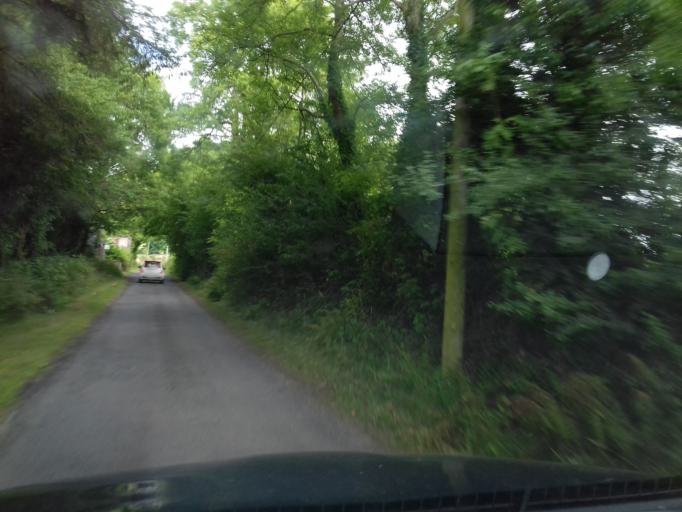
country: IE
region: Leinster
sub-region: Kilkenny
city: Graiguenamanagh
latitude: 52.6165
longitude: -6.8423
